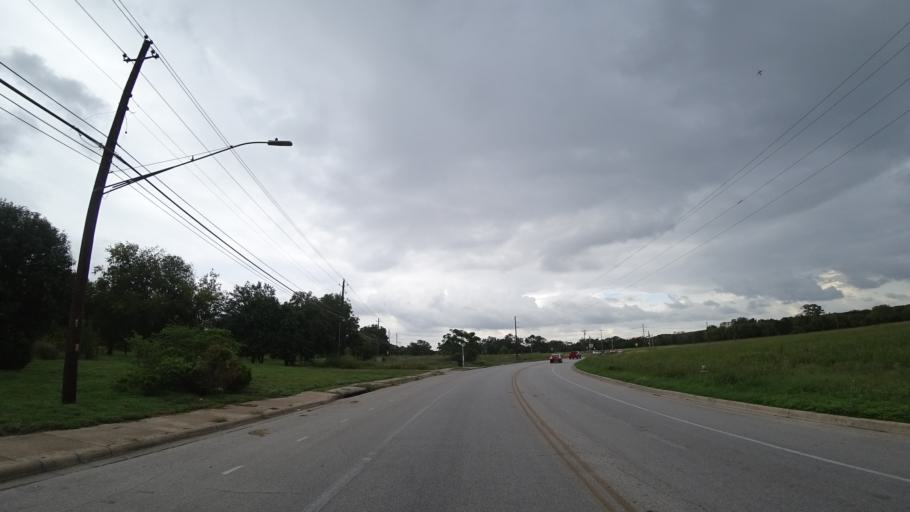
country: US
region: Texas
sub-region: Travis County
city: Onion Creek
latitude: 30.1682
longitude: -97.7399
